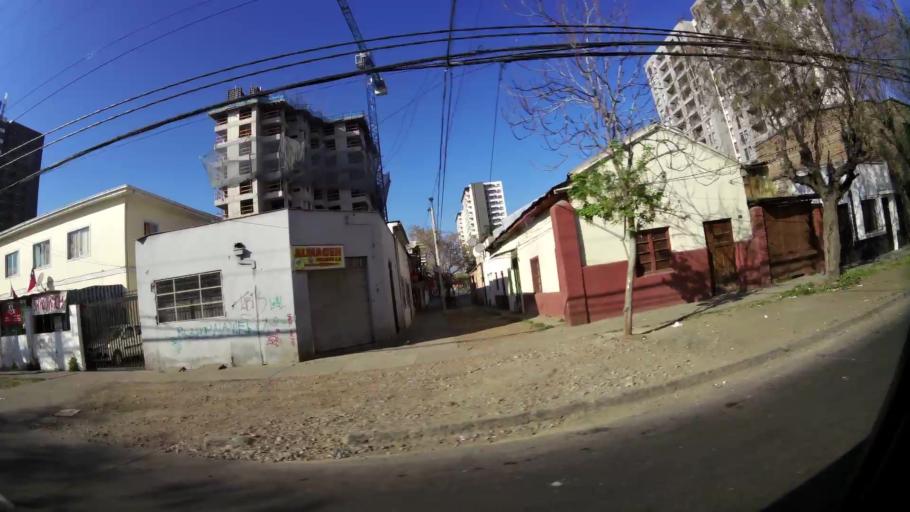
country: CL
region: Santiago Metropolitan
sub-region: Provincia de Santiago
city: Santiago
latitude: -33.4871
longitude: -70.6457
